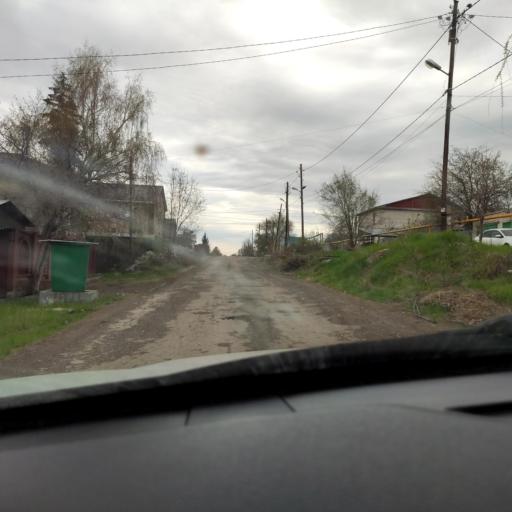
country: RU
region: Samara
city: Petra-Dubrava
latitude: 53.2558
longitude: 50.3439
